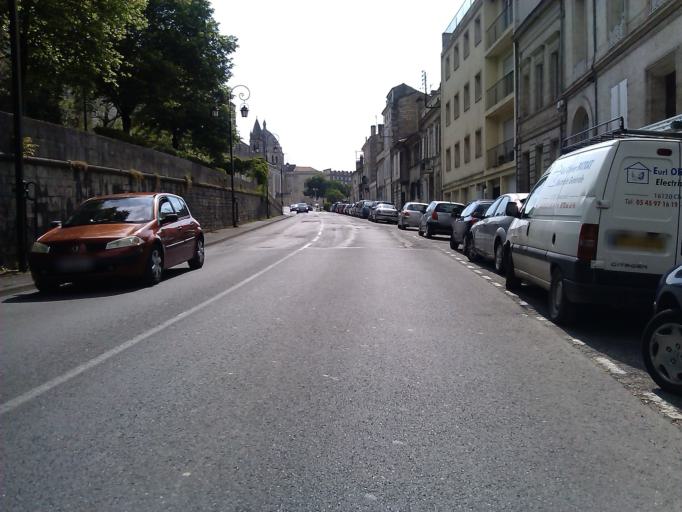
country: FR
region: Poitou-Charentes
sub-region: Departement de la Charente
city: Angouleme
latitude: 45.6494
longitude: 0.1480
